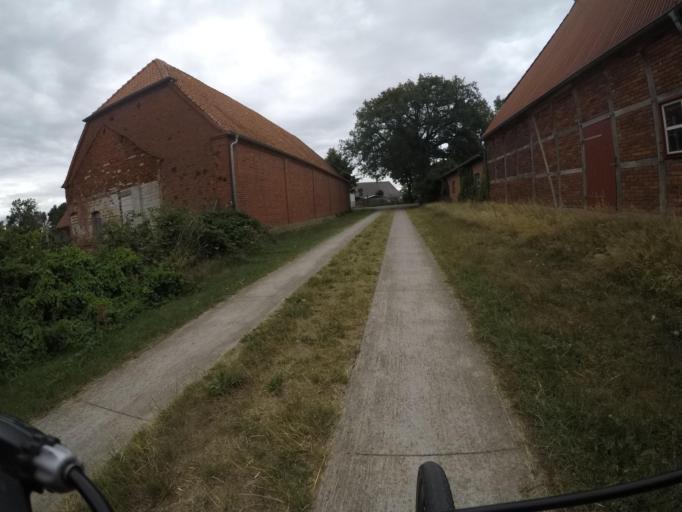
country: DE
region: Lower Saxony
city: Neu Darchau
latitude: 53.2571
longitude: 10.9193
